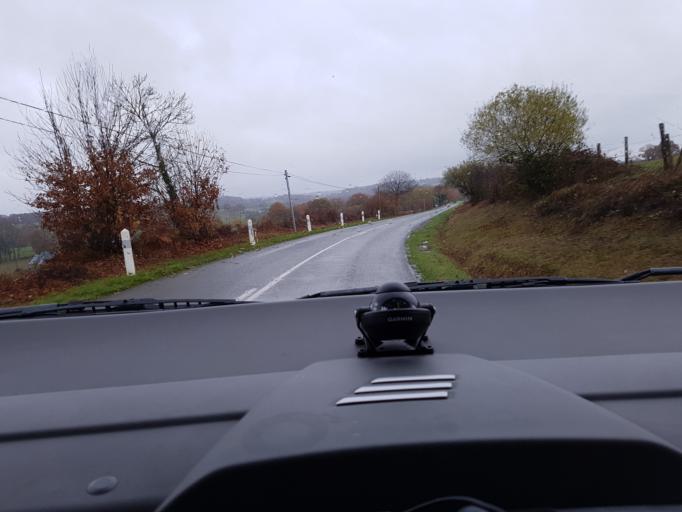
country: FR
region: Pays de la Loire
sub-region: Departement de la Mayenne
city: La Baconniere
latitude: 48.1893
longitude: -0.8767
